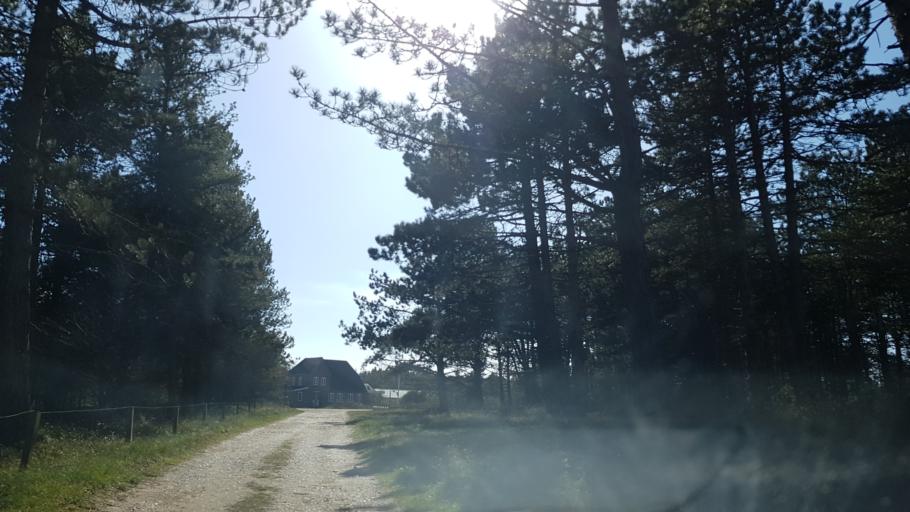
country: DE
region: Schleswig-Holstein
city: List
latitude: 55.0962
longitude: 8.5520
